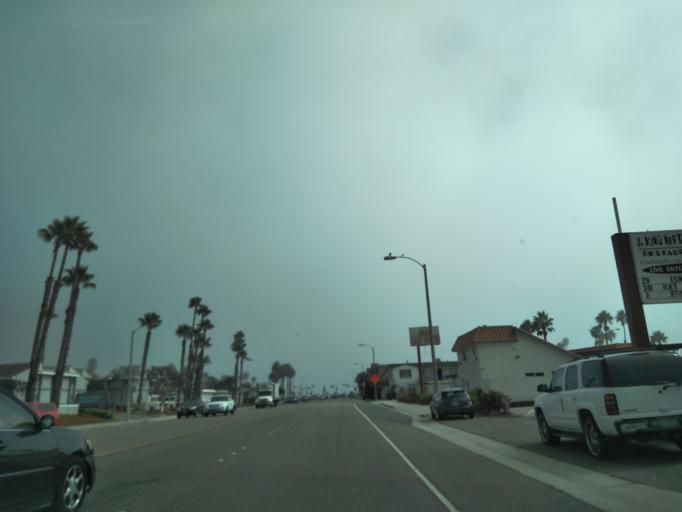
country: US
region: California
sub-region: Orange County
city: Seal Beach
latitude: 33.7135
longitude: -118.0653
